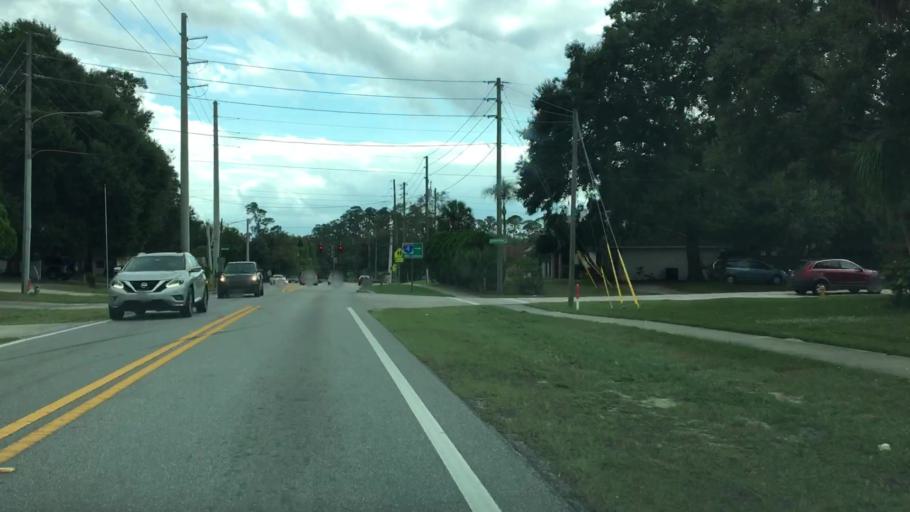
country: US
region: Florida
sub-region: Volusia County
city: Deltona
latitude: 28.8706
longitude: -81.2530
